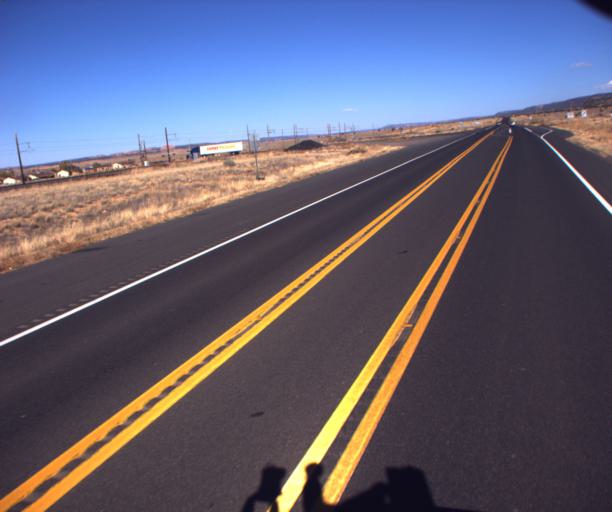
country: US
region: Arizona
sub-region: Coconino County
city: Kaibito
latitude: 36.4604
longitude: -110.6939
